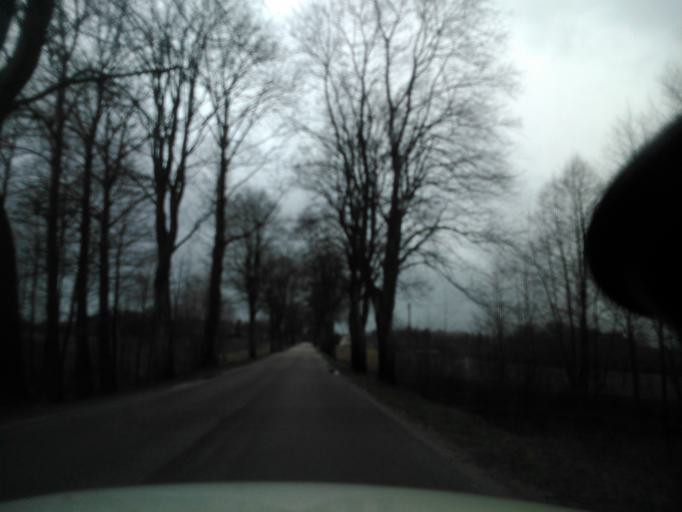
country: PL
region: Warmian-Masurian Voivodeship
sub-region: Powiat ostrodzki
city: Dabrowno
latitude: 53.4690
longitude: 20.0492
